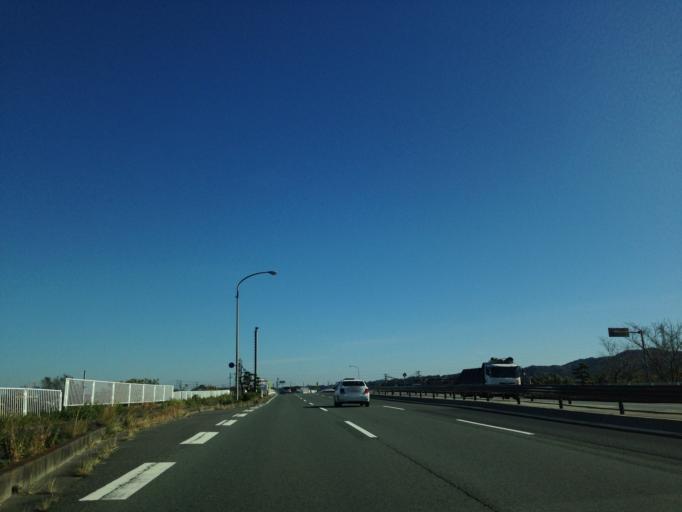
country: JP
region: Shizuoka
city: Fukuroi
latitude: 34.7631
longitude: 137.9607
